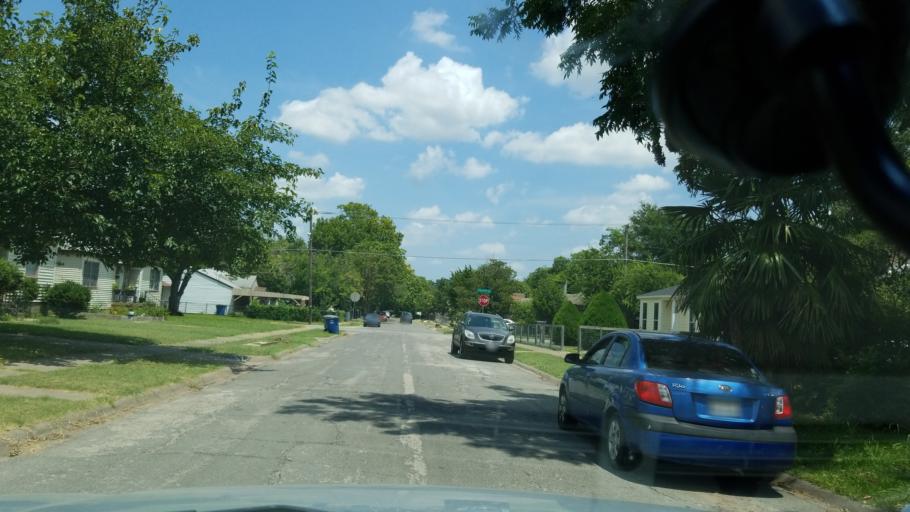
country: US
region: Texas
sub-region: Dallas County
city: Cockrell Hill
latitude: 32.7316
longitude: -96.8723
